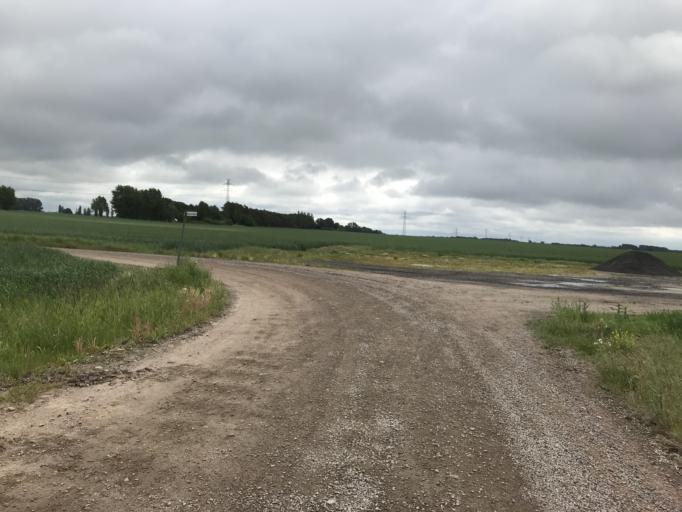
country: SE
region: Skane
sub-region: Landskrona
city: Asmundtorp
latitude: 55.8714
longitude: 12.8958
